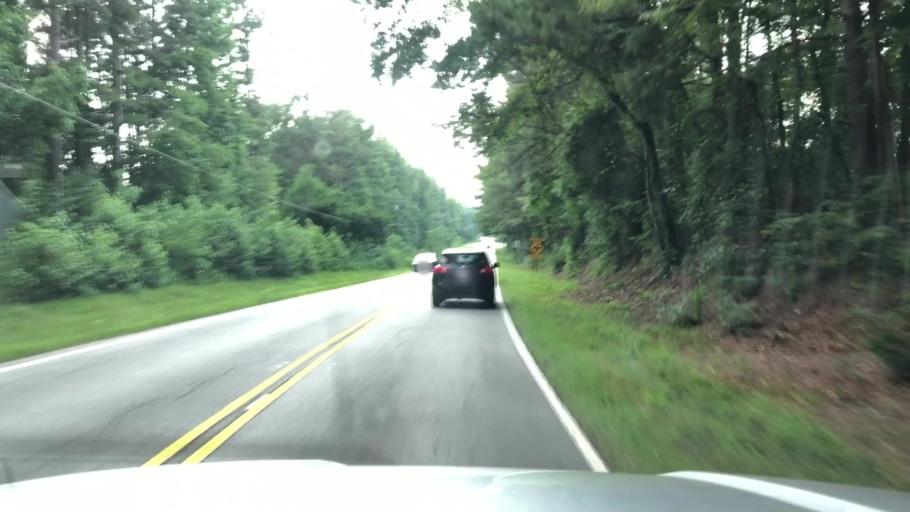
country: US
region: Georgia
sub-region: Paulding County
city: Dallas
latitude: 33.9724
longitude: -84.8123
